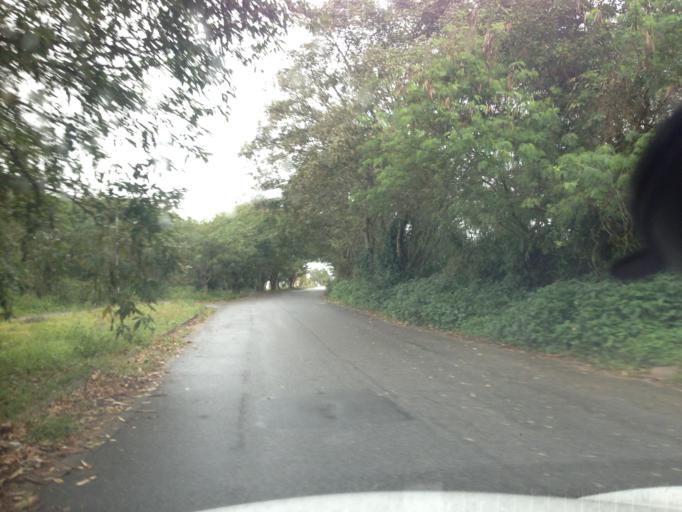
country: BR
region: Sao Paulo
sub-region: Itanhaem
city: Itanhaem
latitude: -24.2321
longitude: -46.8772
